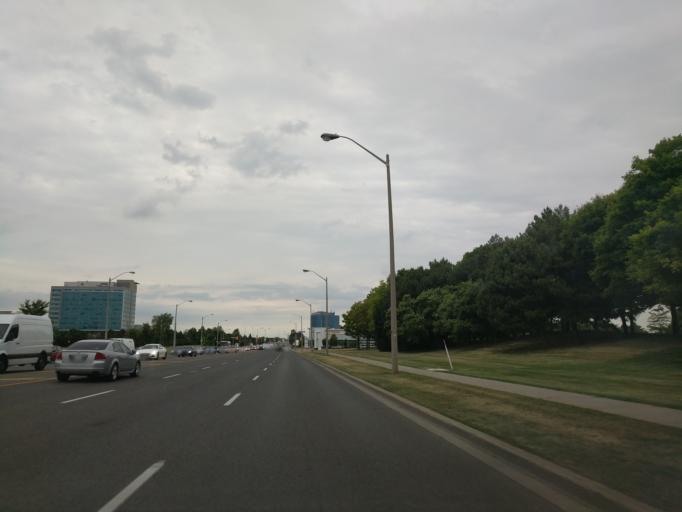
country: CA
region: Ontario
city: Willowdale
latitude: 43.8166
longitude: -79.3382
